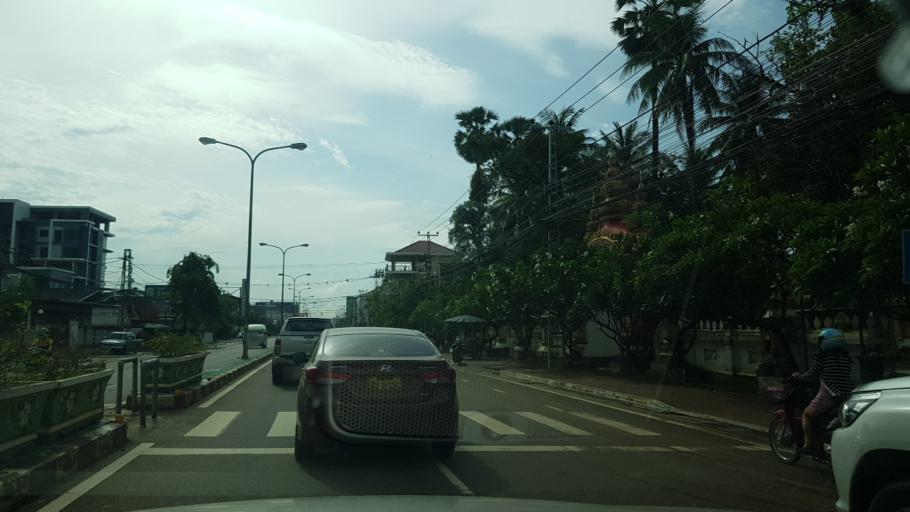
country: TH
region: Nong Khai
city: Si Chiang Mai
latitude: 17.9694
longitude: 102.5804
